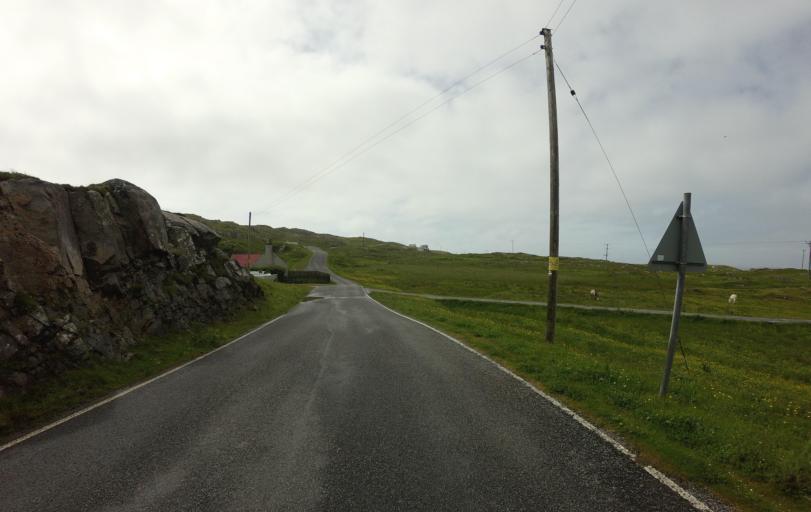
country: GB
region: Scotland
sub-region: Eilean Siar
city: Isle of South Uist
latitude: 57.0822
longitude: -7.3036
